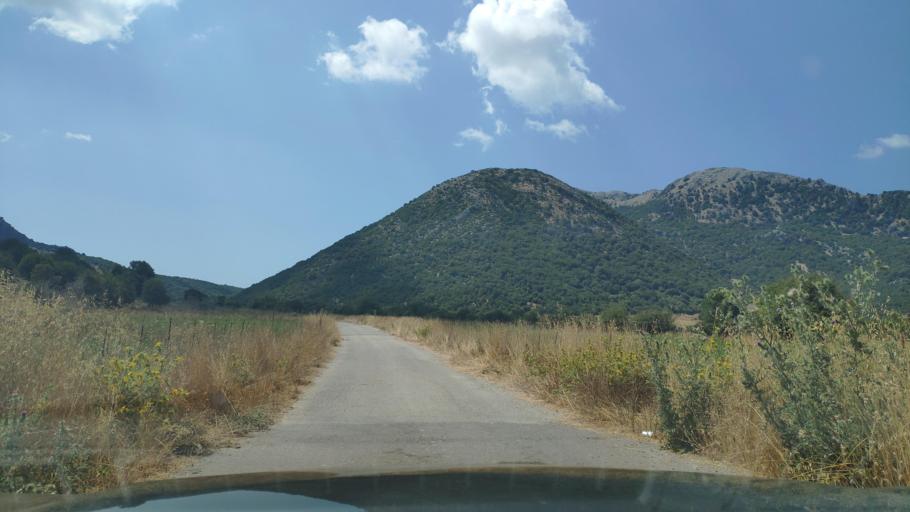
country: GR
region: West Greece
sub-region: Nomos Aitolias kai Akarnanias
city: Monastirakion
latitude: 38.7793
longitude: 20.9721
